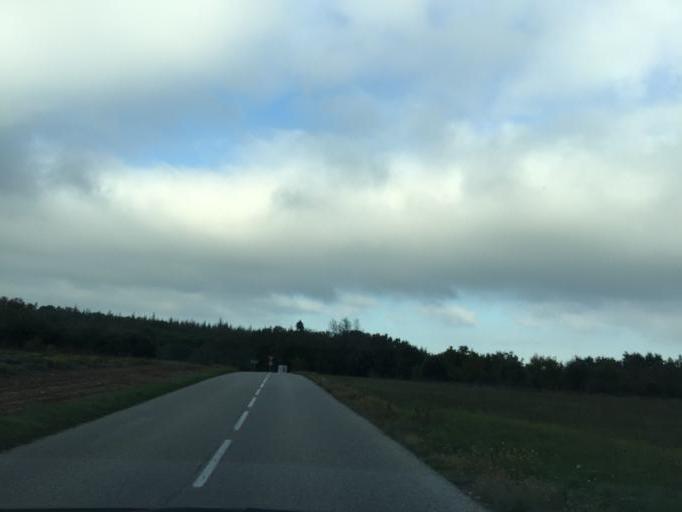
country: FR
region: Rhone-Alpes
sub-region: Departement de la Drome
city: Malataverne
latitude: 44.4858
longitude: 4.7443
